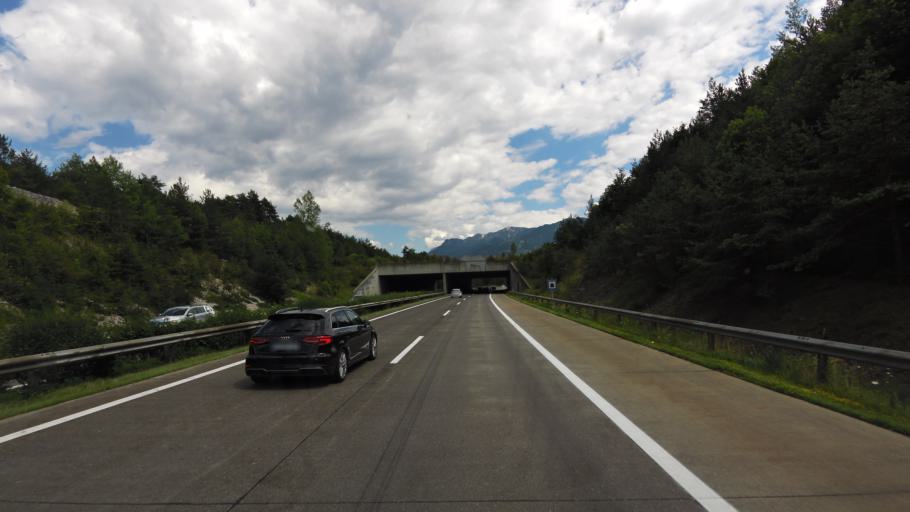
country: AT
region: Carinthia
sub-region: Politischer Bezirk Villach Land
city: Arnoldstein
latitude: 46.5667
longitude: 13.7331
